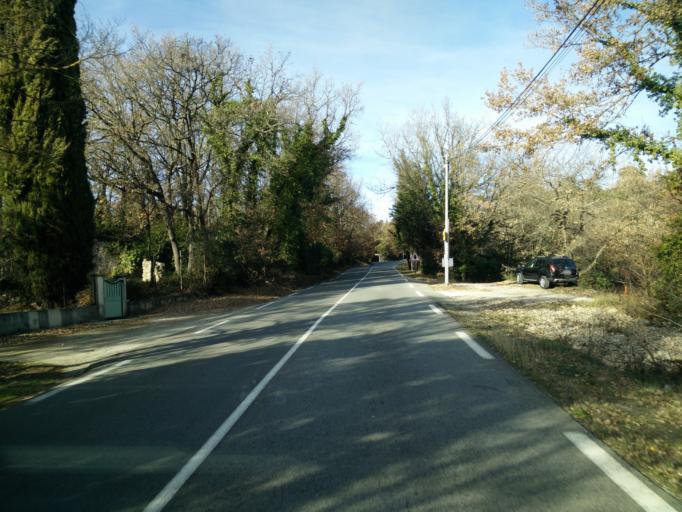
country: FR
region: Provence-Alpes-Cote d'Azur
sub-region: Departement du Var
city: Montauroux
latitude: 43.5944
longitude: 6.7892
